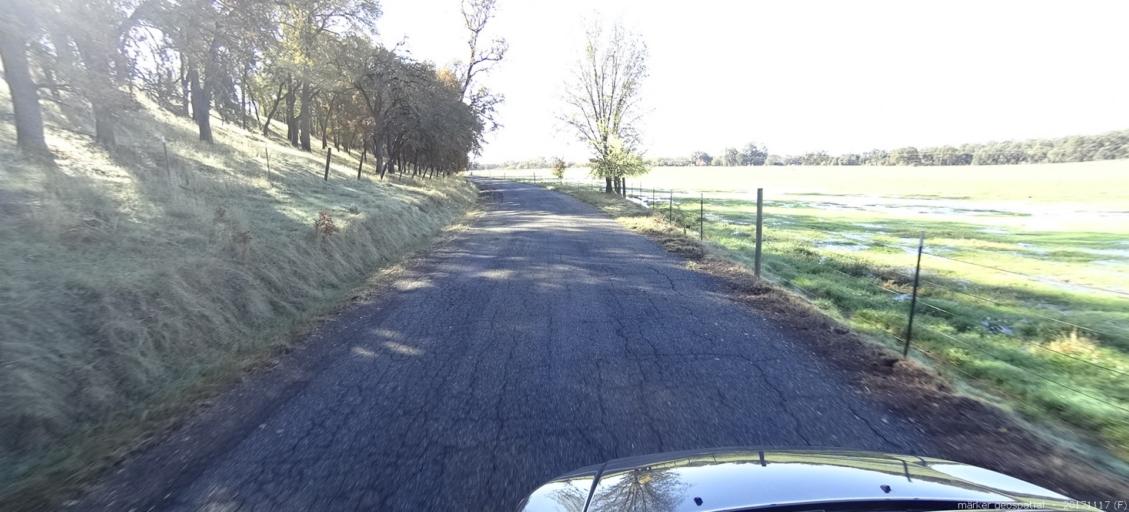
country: US
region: California
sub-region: Shasta County
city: Cottonwood
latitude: 40.4414
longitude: -122.1973
